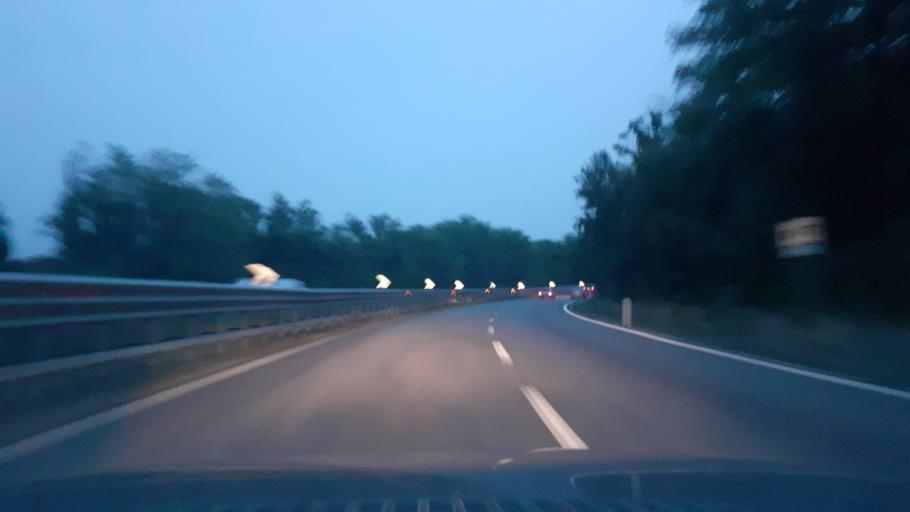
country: IT
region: Lombardy
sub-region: Provincia di Monza e Brianza
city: Briosco
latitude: 45.7039
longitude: 9.2311
